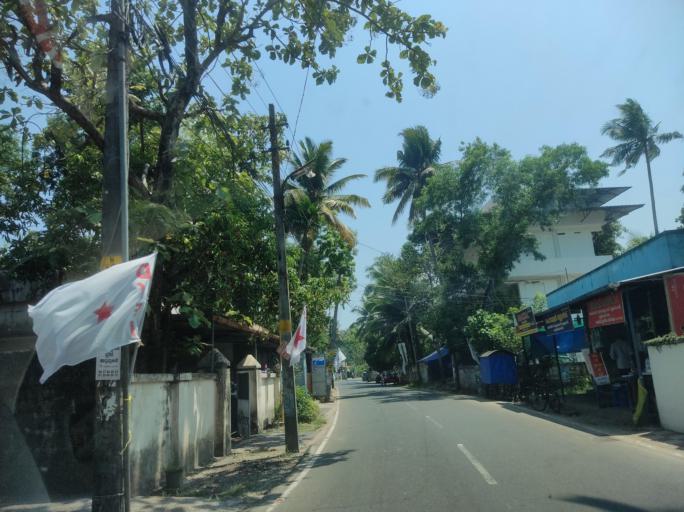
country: IN
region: Kerala
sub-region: Alappuzha
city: Arukutti
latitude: 9.8549
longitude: 76.2936
